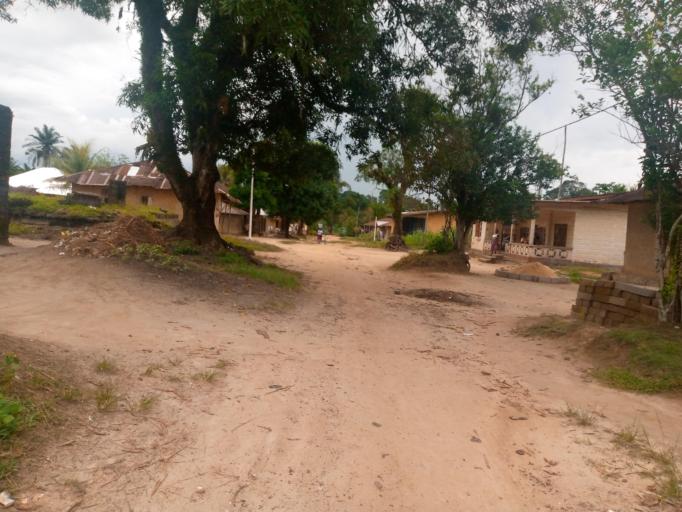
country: SL
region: Southern Province
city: Mogbwemo
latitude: 7.6064
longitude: -12.1748
